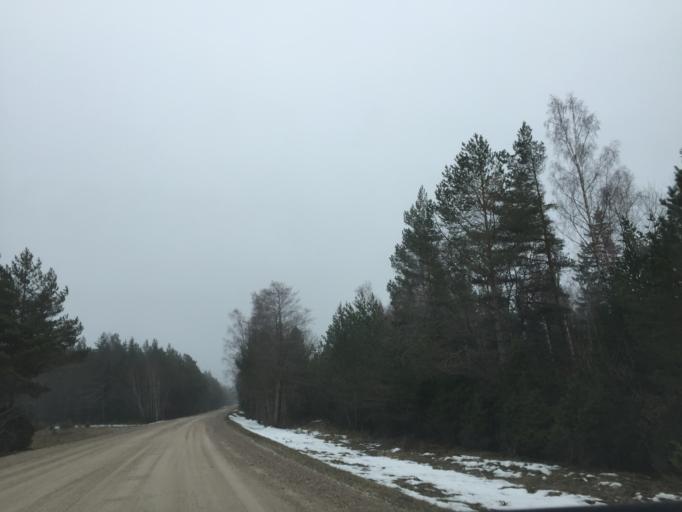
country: EE
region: Saare
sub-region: Kuressaare linn
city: Kuressaare
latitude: 58.4841
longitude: 21.9967
